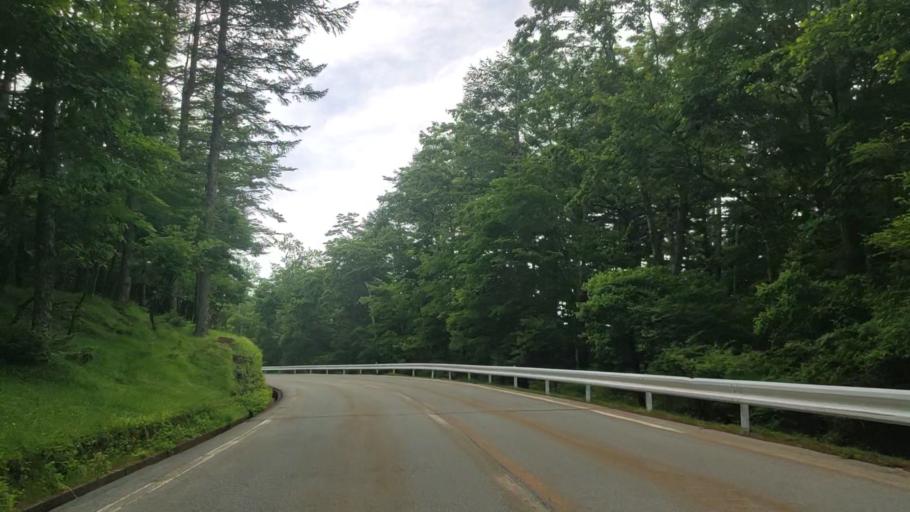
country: JP
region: Yamanashi
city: Fujikawaguchiko
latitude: 35.4164
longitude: 138.7293
